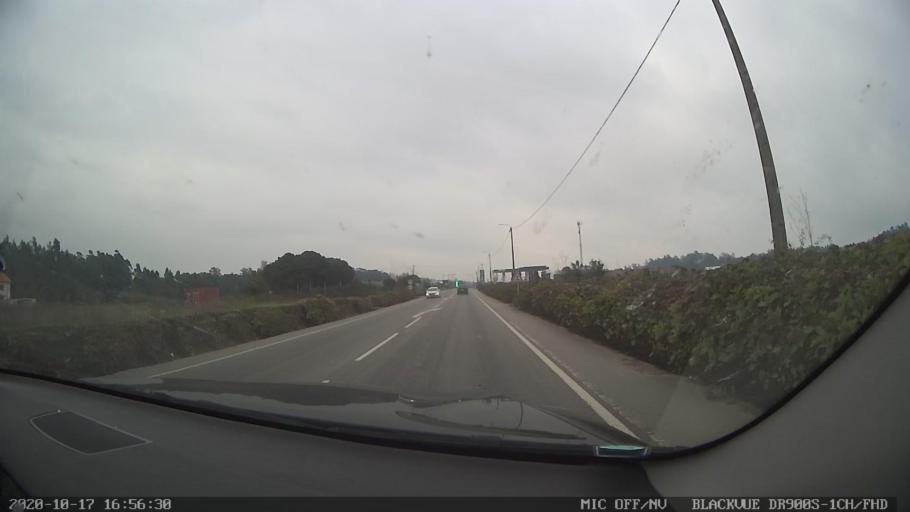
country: PT
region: Braga
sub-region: Esposende
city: Apulia
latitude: 41.5060
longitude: -8.7641
